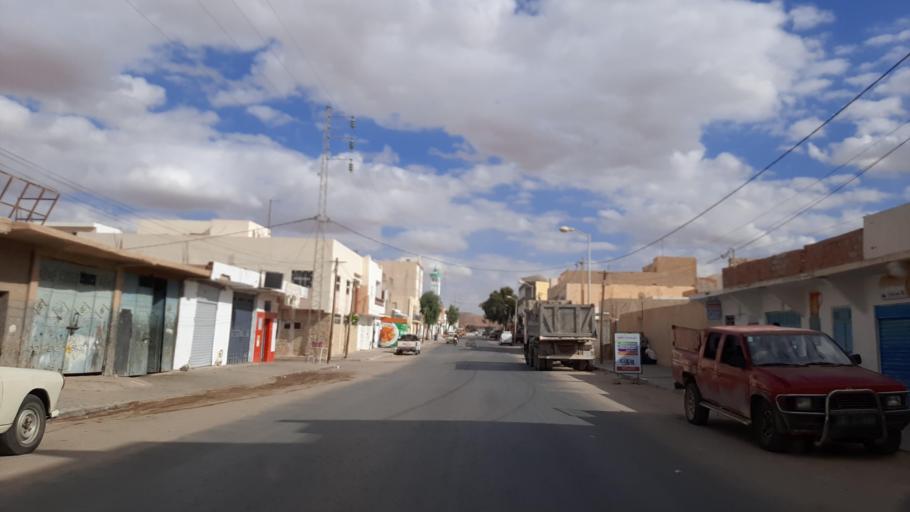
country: TN
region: Tataouine
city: Tataouine
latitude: 32.9210
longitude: 10.4629
